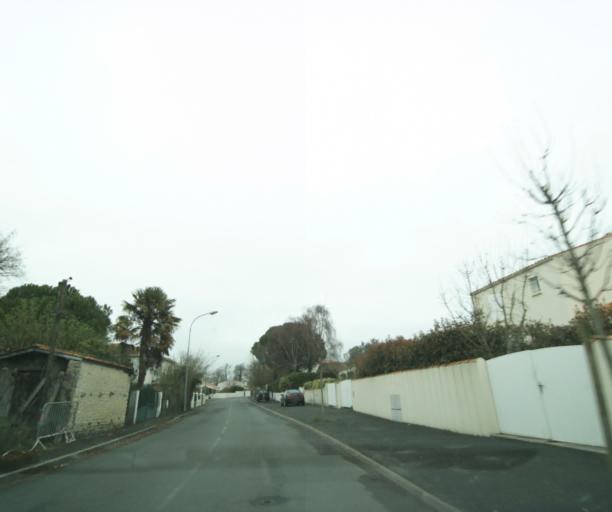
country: FR
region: Poitou-Charentes
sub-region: Departement de la Charente-Maritime
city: Lagord
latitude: 46.1874
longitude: -1.1402
